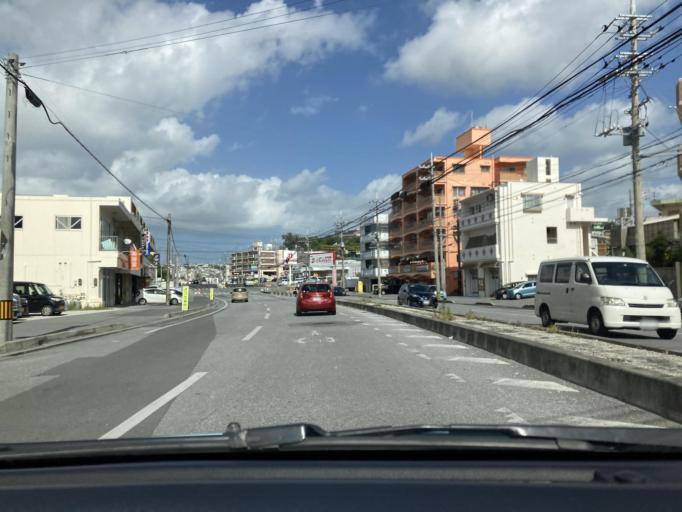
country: JP
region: Okinawa
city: Tomigusuku
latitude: 26.1903
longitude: 127.6912
